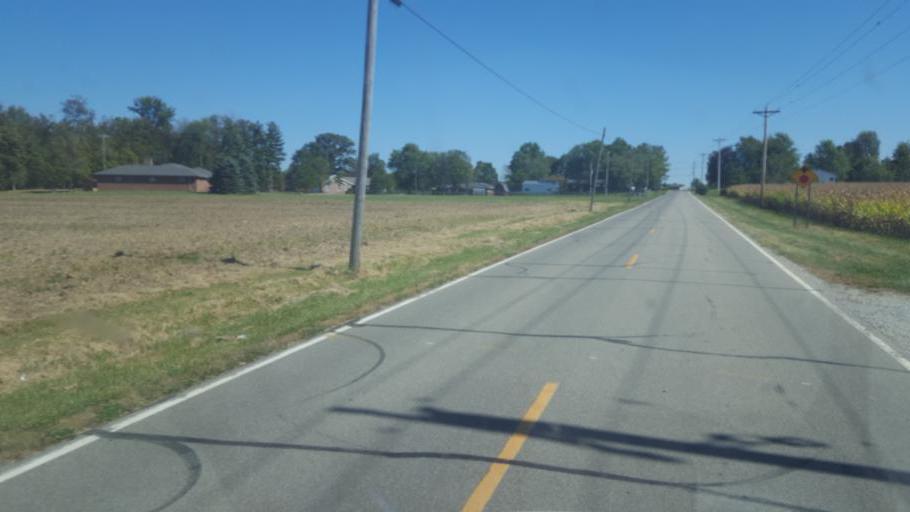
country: US
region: Ohio
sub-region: Huron County
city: Willard
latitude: 40.9508
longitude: -82.8572
